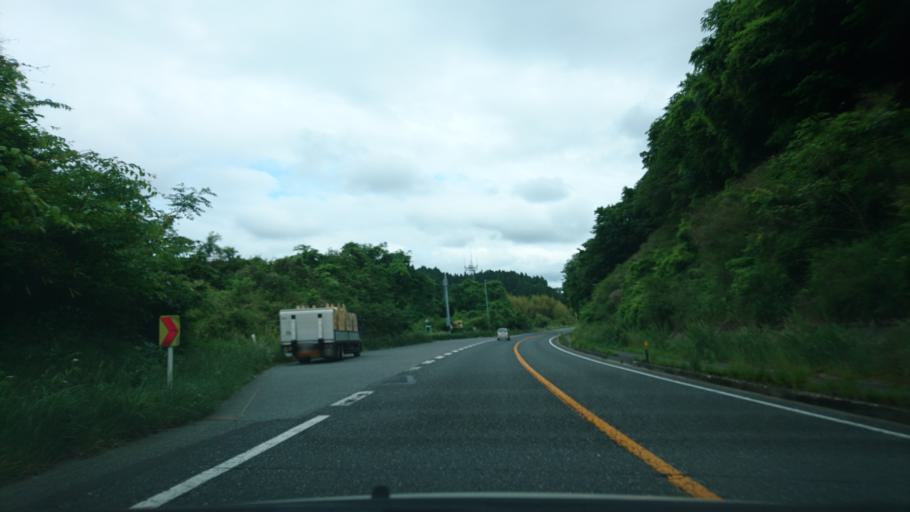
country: JP
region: Iwate
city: Ichinoseki
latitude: 38.8986
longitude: 141.1138
